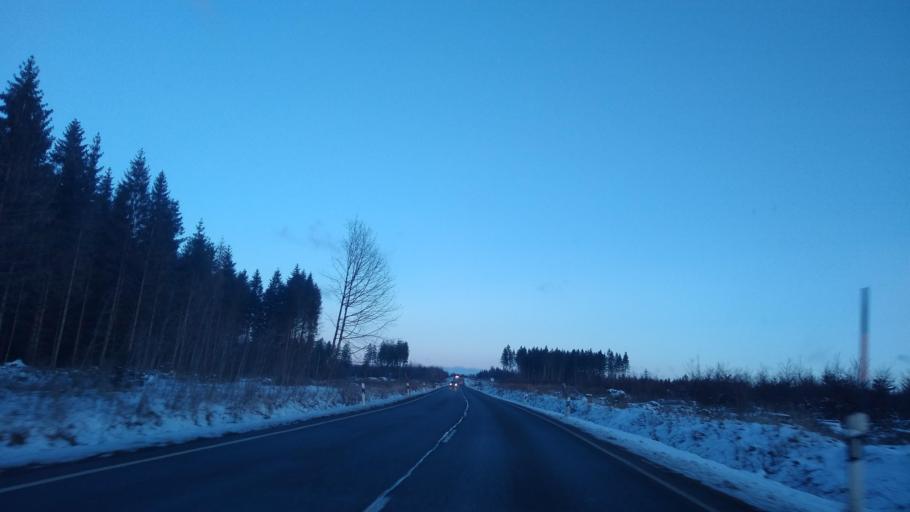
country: DE
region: Lower Saxony
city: Clausthal-Zellerfeld
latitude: 51.7903
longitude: 10.3686
